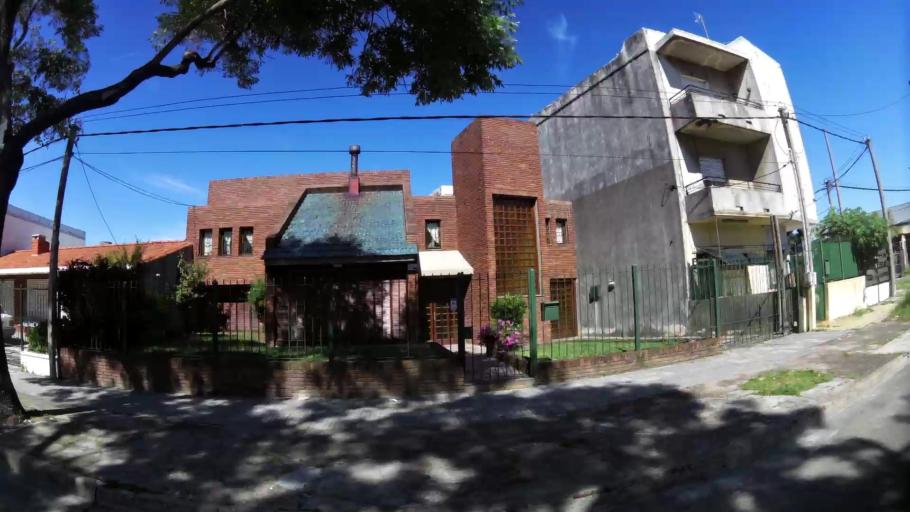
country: UY
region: Montevideo
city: Montevideo
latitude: -34.8912
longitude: -56.1421
